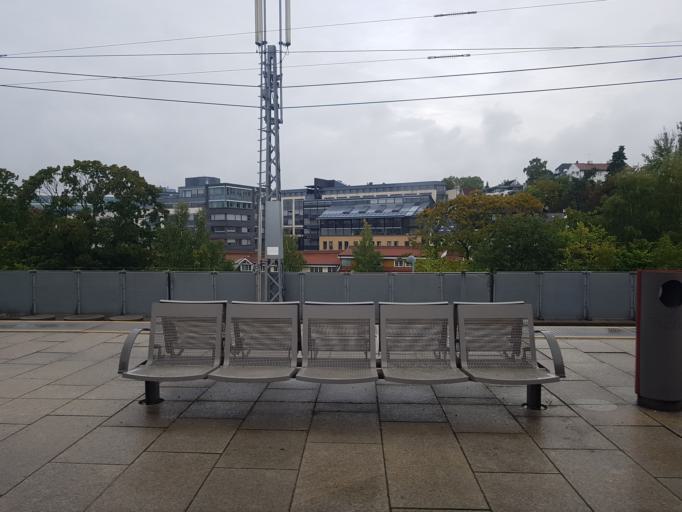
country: NO
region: Akershus
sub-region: Baerum
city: Lysaker
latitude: 59.9184
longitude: 10.6546
